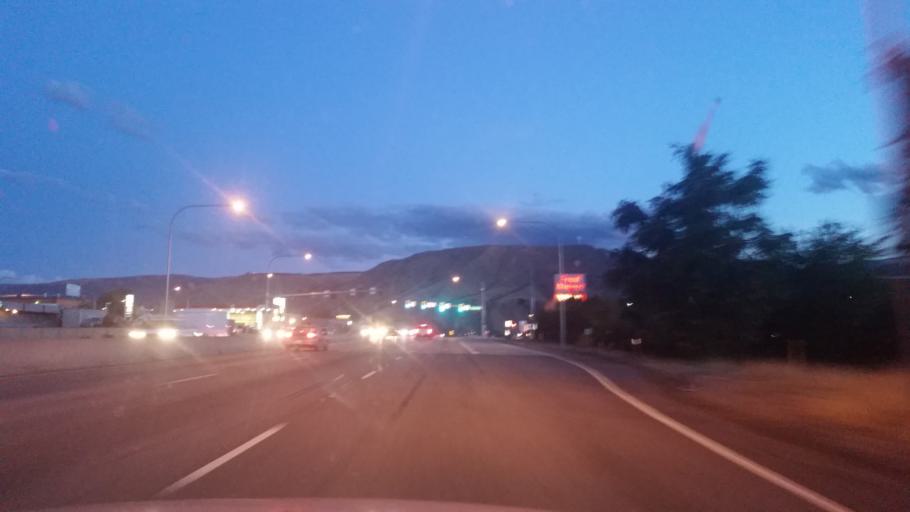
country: US
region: Washington
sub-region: Douglas County
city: East Wenatchee
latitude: 47.4073
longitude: -120.2899
